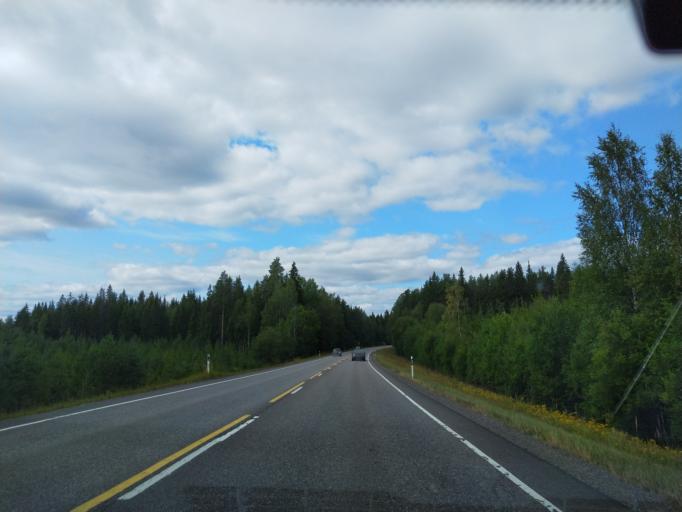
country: FI
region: Haeme
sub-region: Riihimaeki
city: Loppi
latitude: 60.7487
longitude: 24.3265
